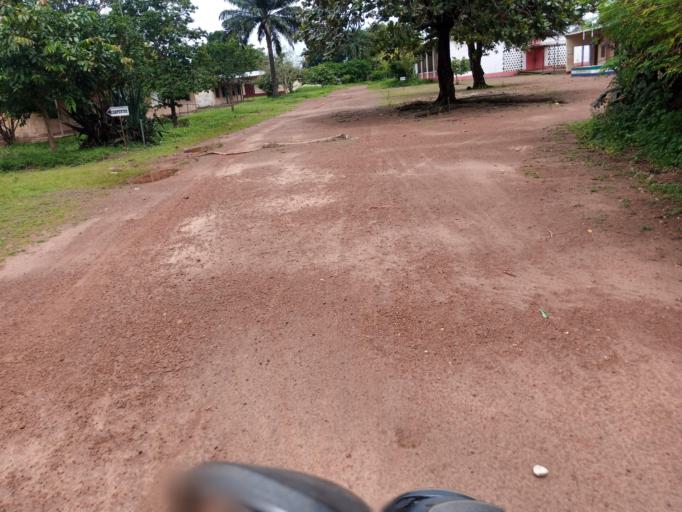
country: SL
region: Southern Province
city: Largo
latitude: 8.1979
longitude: -12.0629
